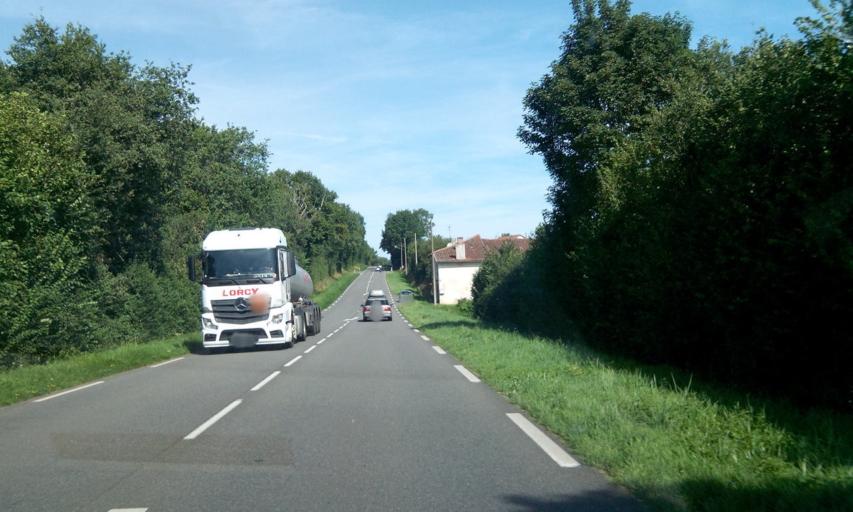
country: FR
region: Poitou-Charentes
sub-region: Departement de la Charente
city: Confolens
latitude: 45.9667
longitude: 0.6965
